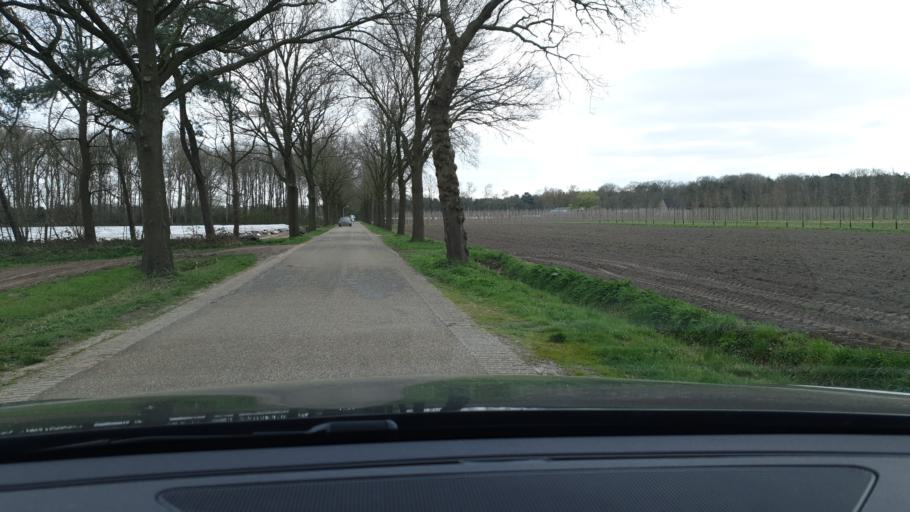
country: NL
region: North Brabant
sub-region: Gemeente Oirschot
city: Oirschot
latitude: 51.4984
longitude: 5.3371
